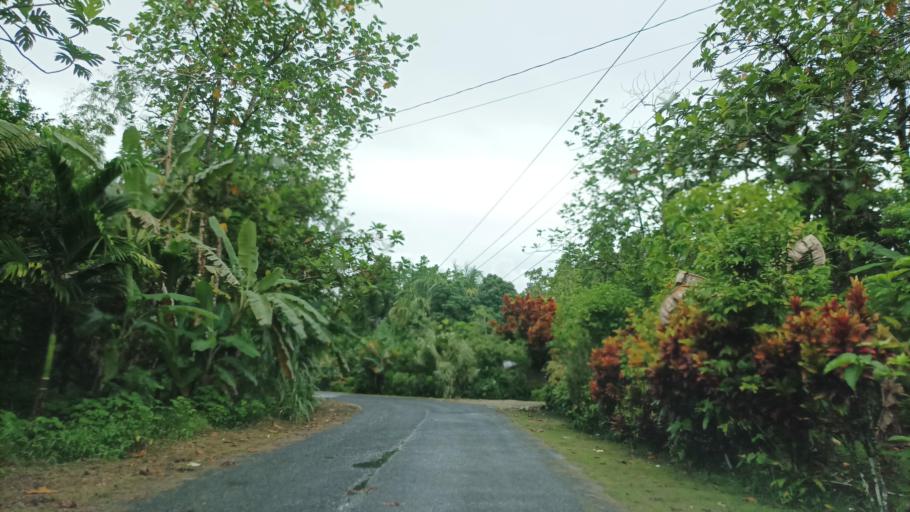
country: FM
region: Pohnpei
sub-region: Sokehs Municipality
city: Palikir - National Government Center
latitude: 6.8443
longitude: 158.1574
